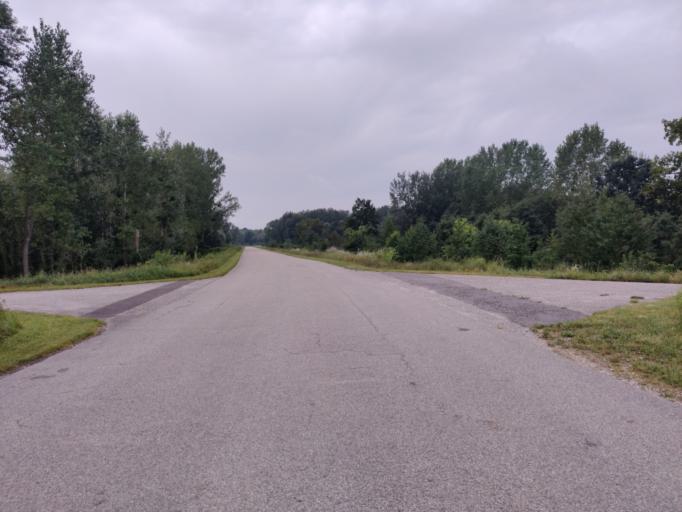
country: AT
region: Upper Austria
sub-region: Politischer Bezirk Linz-Land
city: Asten
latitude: 48.2415
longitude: 14.4248
